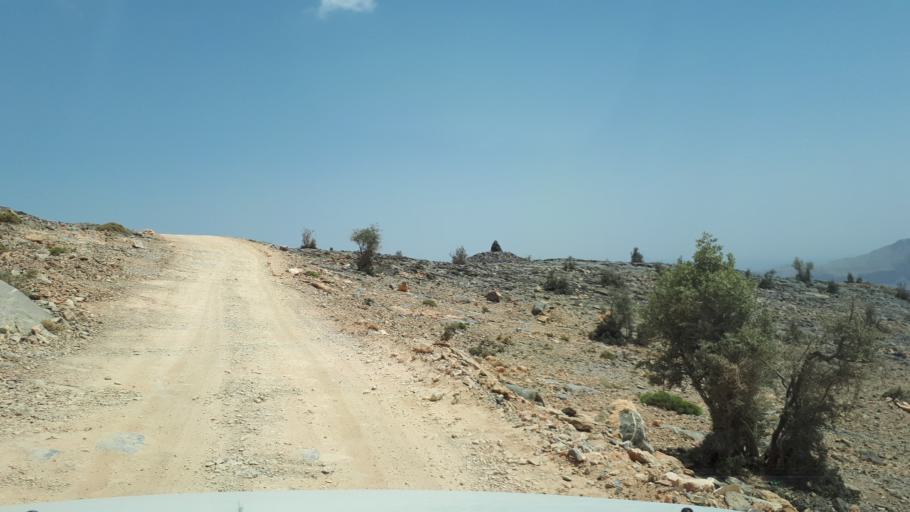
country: OM
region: Muhafazat ad Dakhiliyah
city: Bahla'
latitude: 23.1942
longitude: 57.1966
